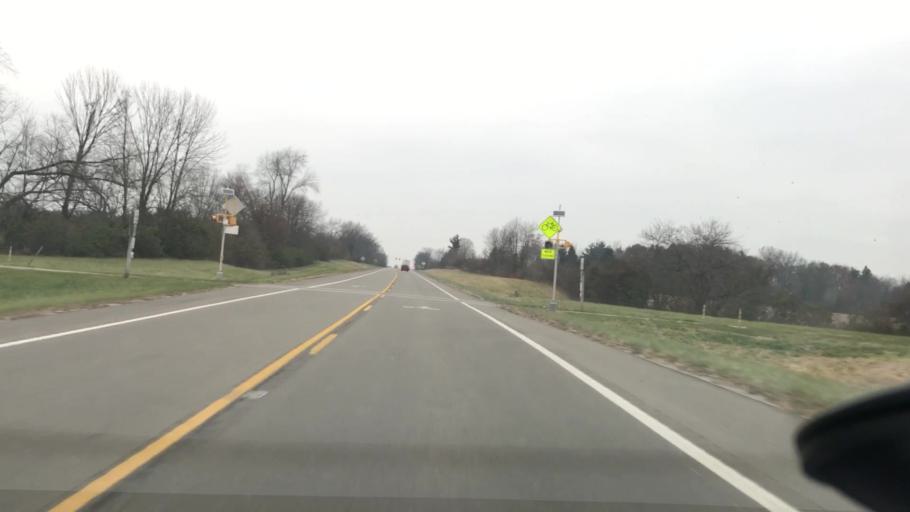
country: US
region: Ohio
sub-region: Clark County
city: Springfield
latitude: 39.8756
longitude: -83.8453
